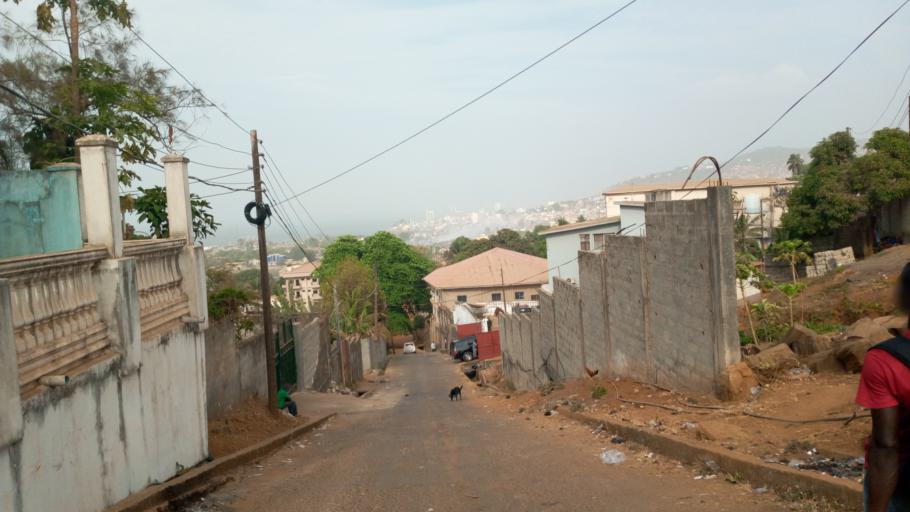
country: SL
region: Western Area
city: Freetown
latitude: 8.4814
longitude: -13.2652
